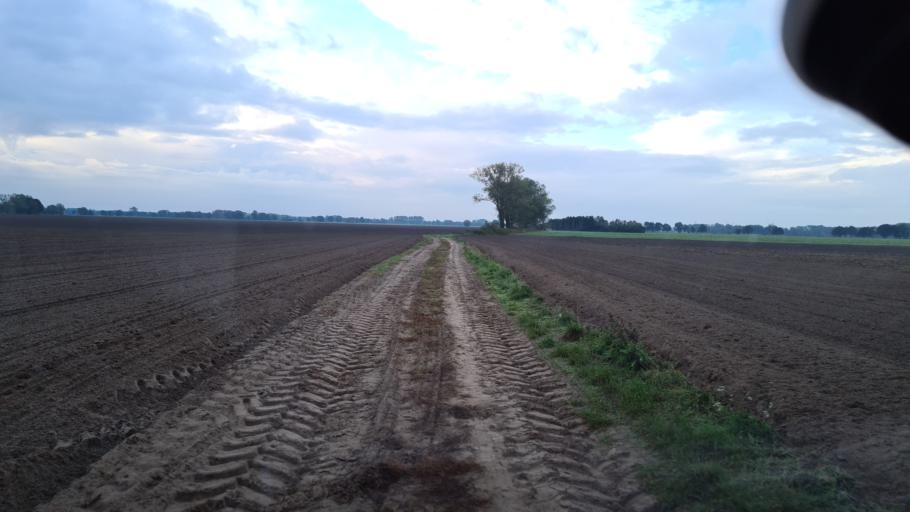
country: DE
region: Brandenburg
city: Schonewalde
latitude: 51.6912
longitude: 13.5690
